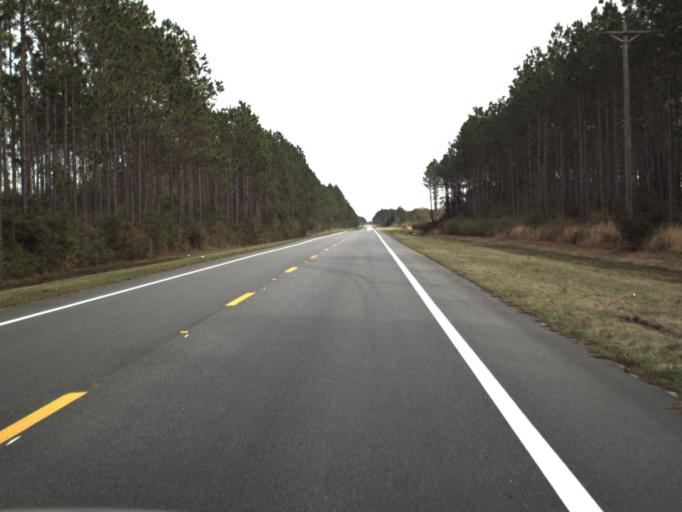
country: US
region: Florida
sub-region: Bay County
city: Callaway
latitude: 30.1423
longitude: -85.4173
